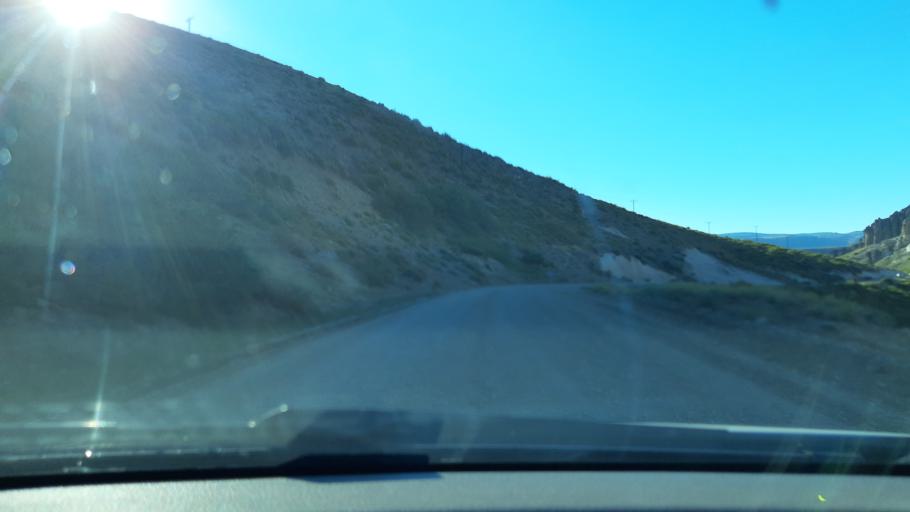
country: AR
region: Neuquen
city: Las Ovejas
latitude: -36.8080
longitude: -70.7219
